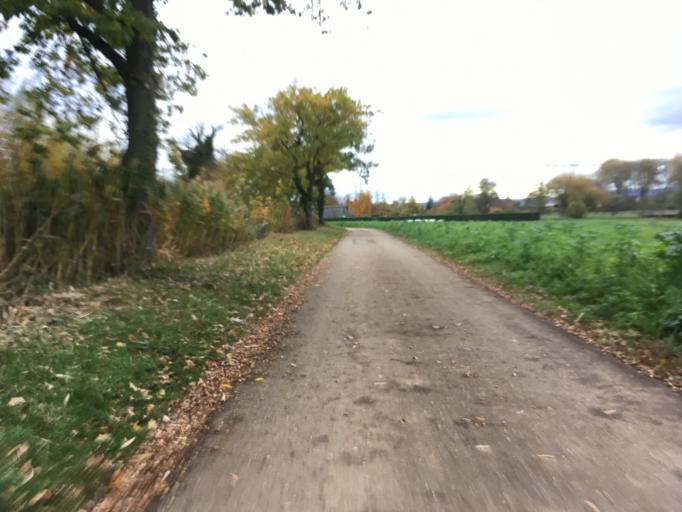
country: DE
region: Baden-Wuerttemberg
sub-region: Freiburg Region
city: Eichstetten
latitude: 48.0892
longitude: 7.7456
